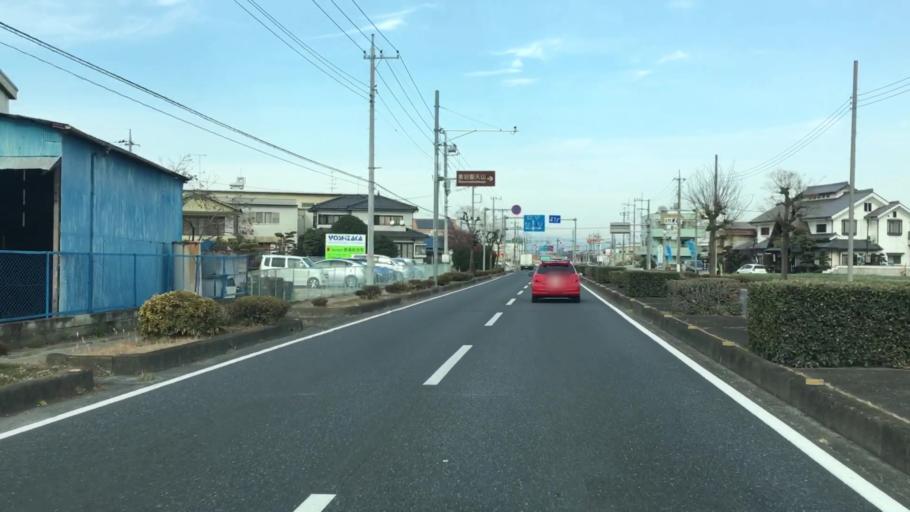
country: JP
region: Saitama
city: Menuma
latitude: 36.2260
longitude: 139.3699
